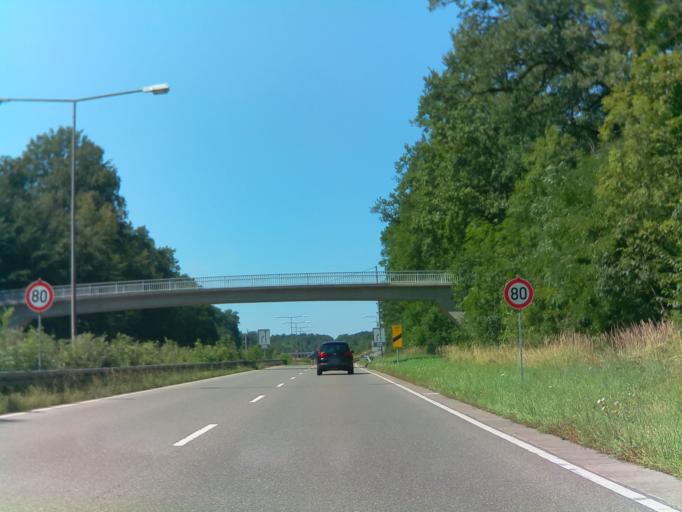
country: DE
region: Baden-Wuerttemberg
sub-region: Regierungsbezirk Stuttgart
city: Gerlingen
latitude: 48.7756
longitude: 9.0956
